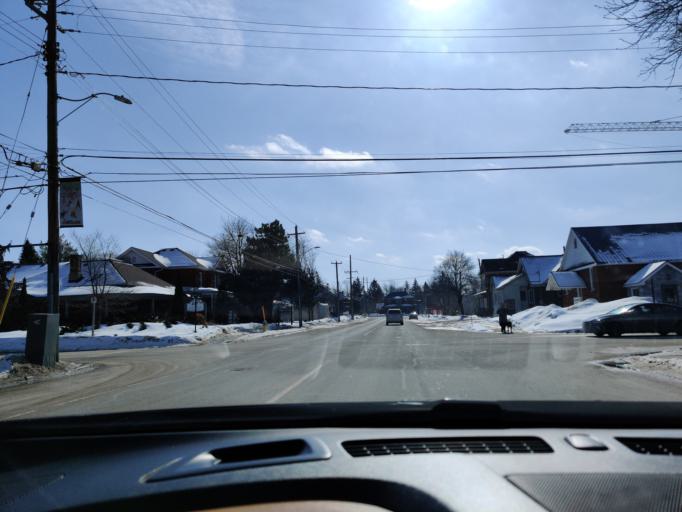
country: CA
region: Ontario
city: Collingwood
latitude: 44.4975
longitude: -80.2146
